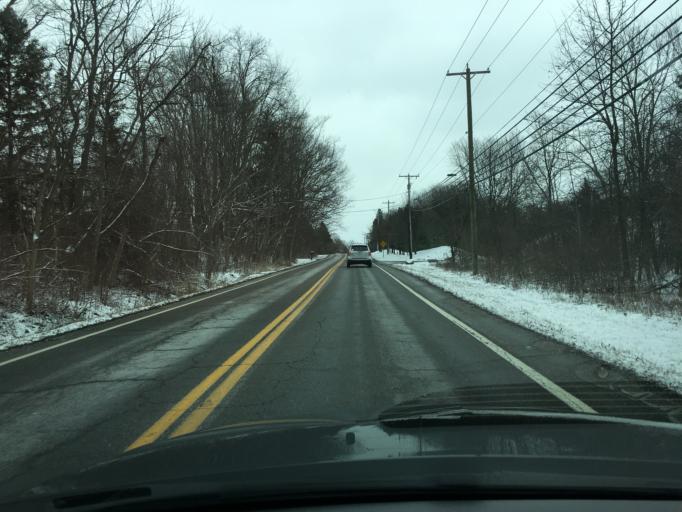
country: US
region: Ohio
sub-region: Summit County
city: Fairlawn
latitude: 41.1396
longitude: -81.5950
